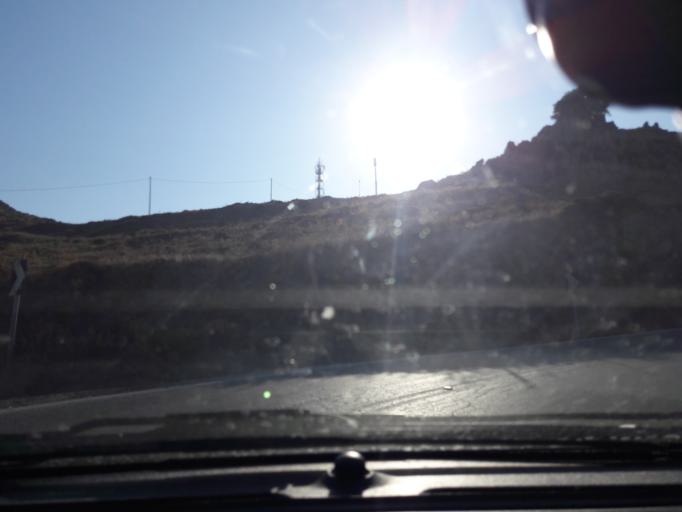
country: GR
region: North Aegean
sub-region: Nomos Lesvou
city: Myrina
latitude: 39.8599
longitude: 25.0796
